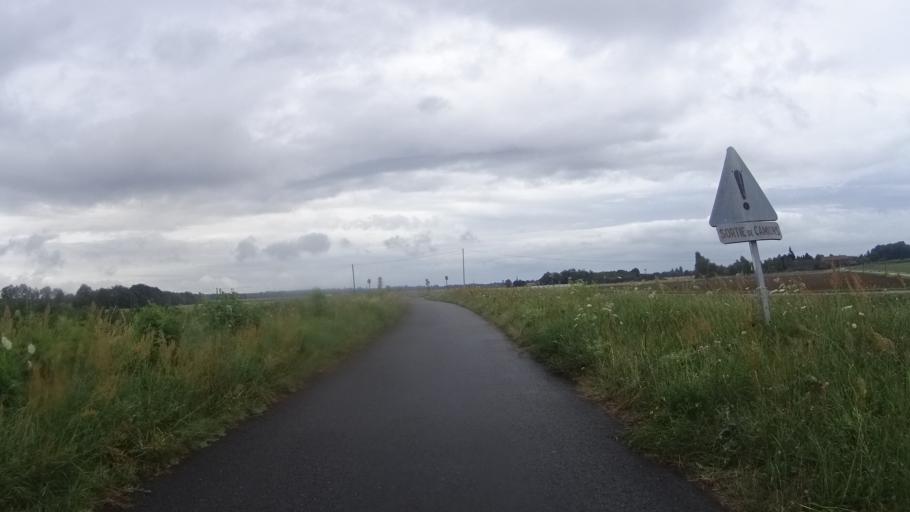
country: FR
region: Centre
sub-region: Departement du Loiret
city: Mardie
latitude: 47.8570
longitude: 2.0657
